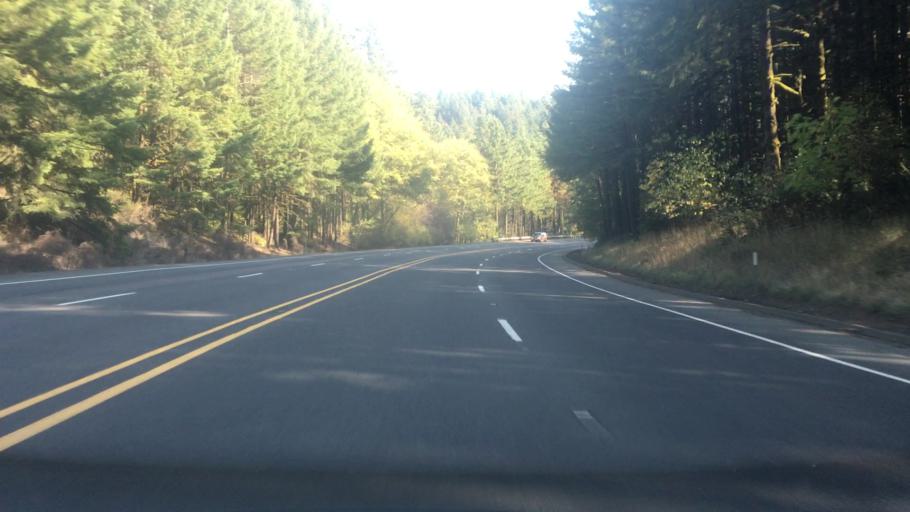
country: US
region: Oregon
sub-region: Polk County
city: Grand Ronde
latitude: 45.0610
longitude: -123.6918
